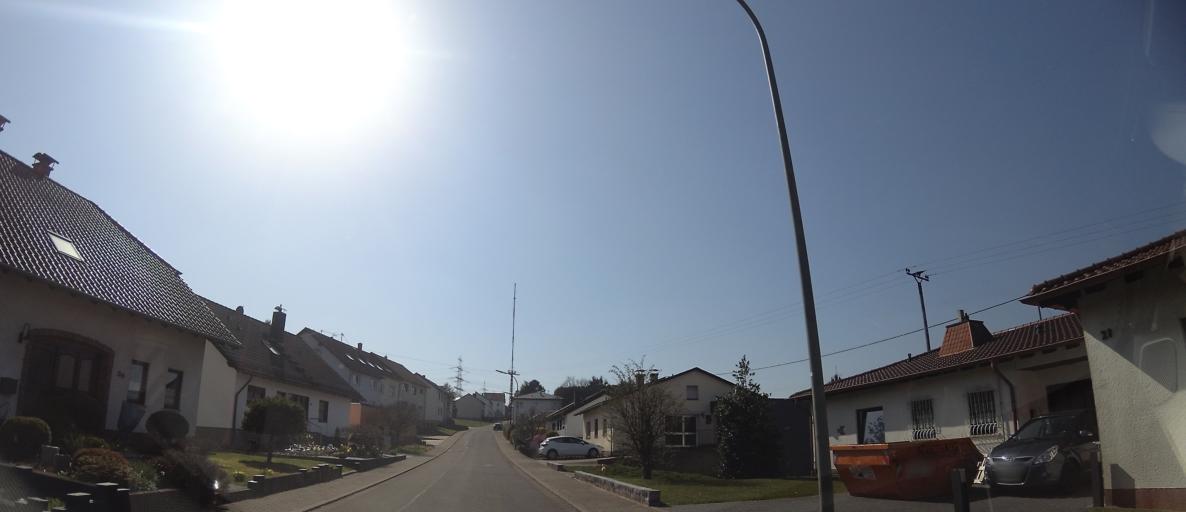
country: DE
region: Saarland
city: Merchweiler
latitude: 49.3441
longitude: 7.0246
